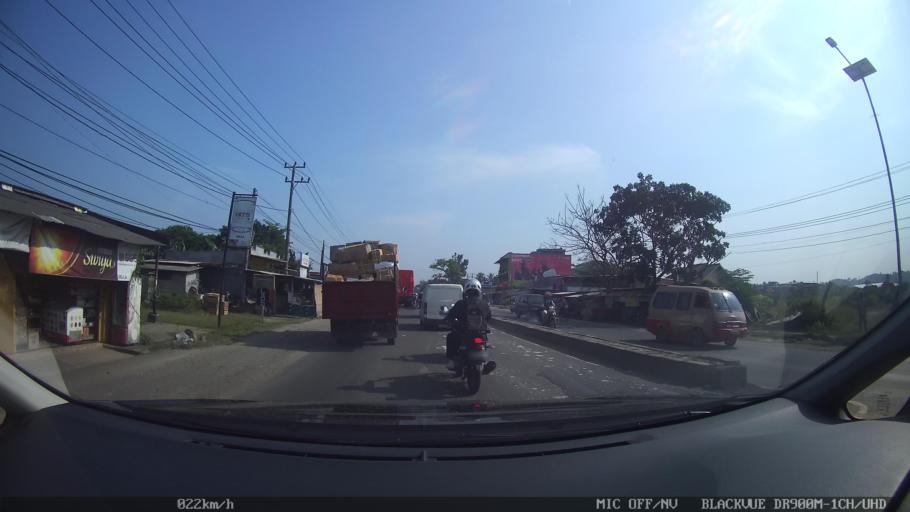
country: ID
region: Lampung
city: Natar
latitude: -5.2995
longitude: 105.1919
